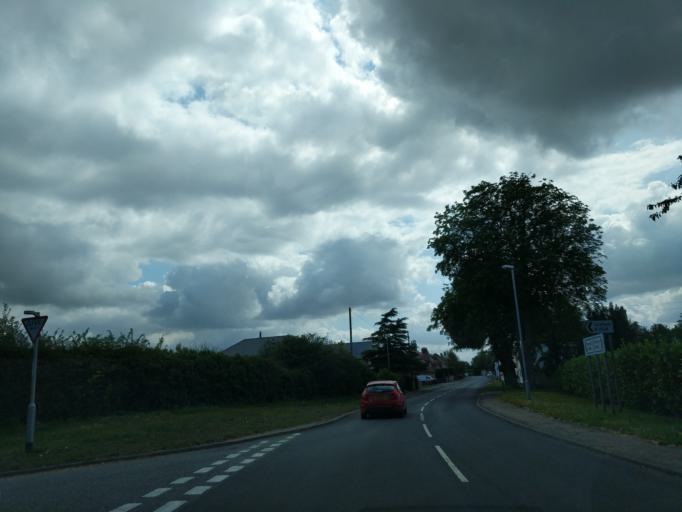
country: GB
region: England
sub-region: Cambridgeshire
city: Isleham
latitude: 52.3040
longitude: 0.4341
